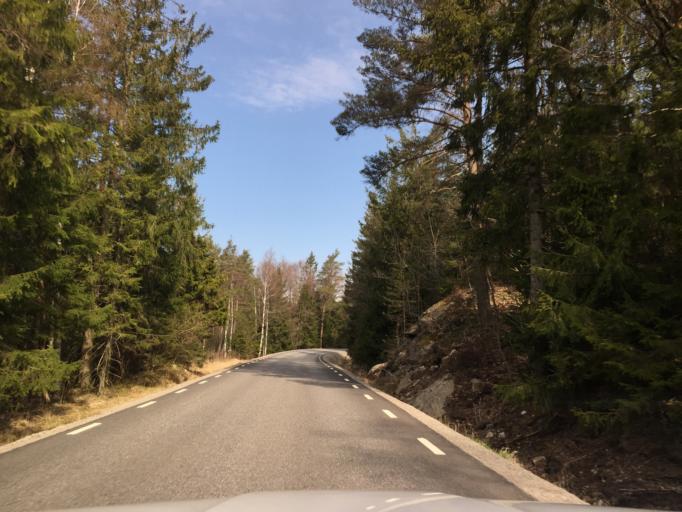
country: SE
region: Vaestra Goetaland
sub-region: Lilla Edets Kommun
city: Lilla Edet
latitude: 58.0847
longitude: 12.0366
